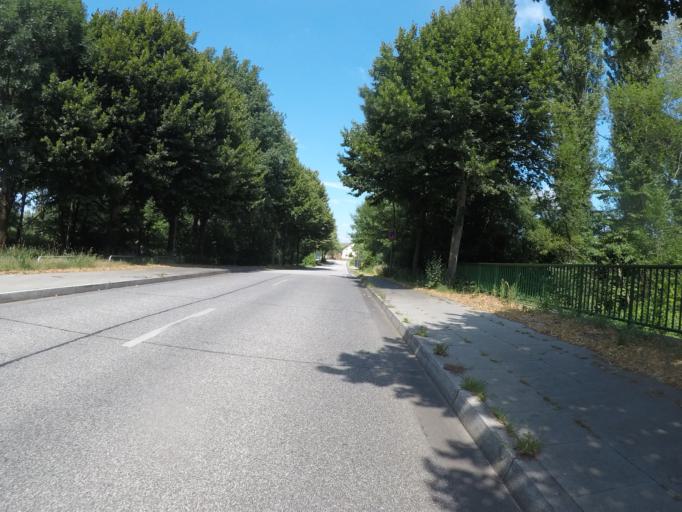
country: DE
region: Hamburg
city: Rothenburgsort
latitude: 53.5023
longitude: 10.0269
